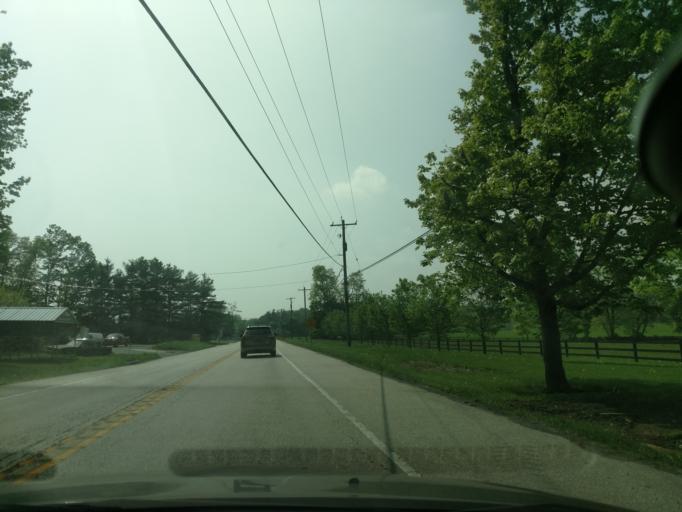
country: US
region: Pennsylvania
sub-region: Chester County
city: Elverson
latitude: 40.1631
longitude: -75.7616
